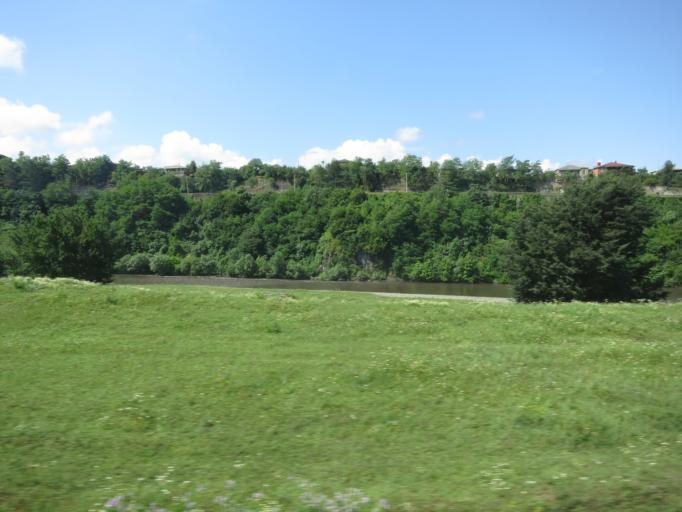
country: GE
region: Imereti
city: Zestap'oni
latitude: 42.1036
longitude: 43.0583
